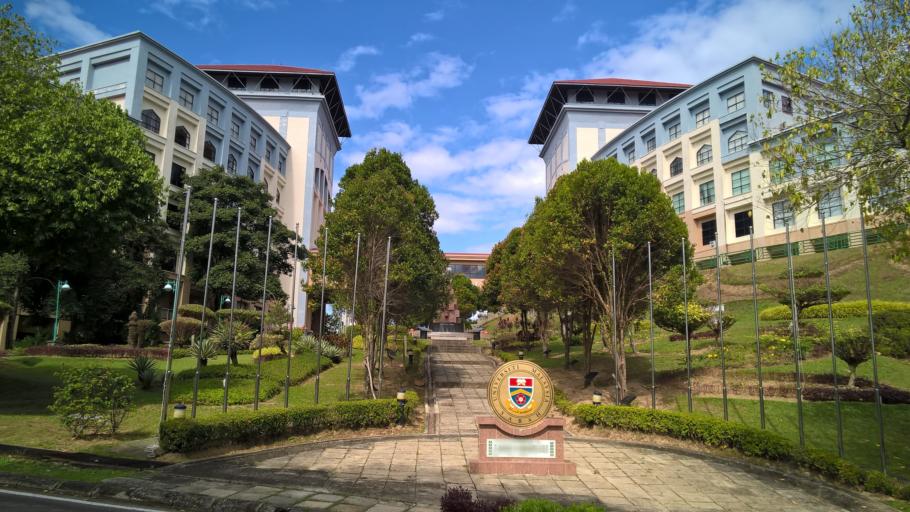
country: MY
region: Sabah
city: Kota Kinabalu
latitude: 6.0361
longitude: 116.1162
